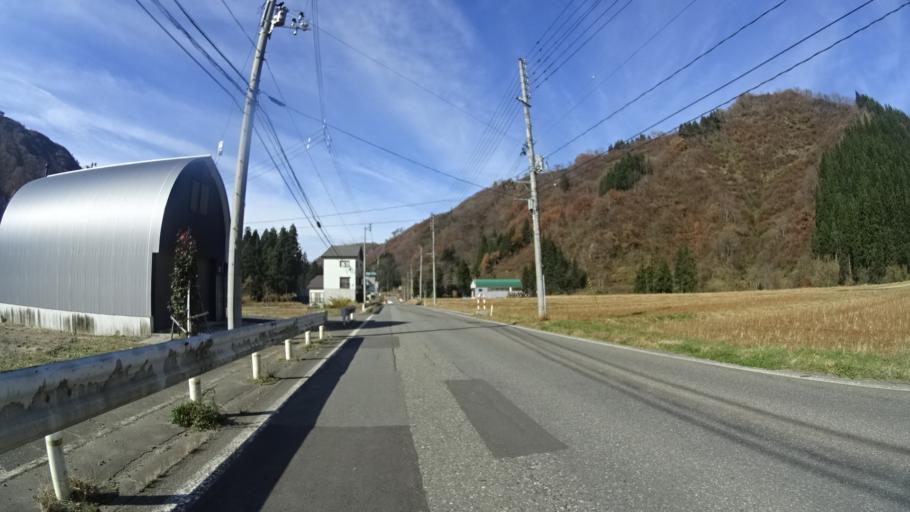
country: JP
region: Niigata
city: Muikamachi
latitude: 37.2176
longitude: 139.0353
